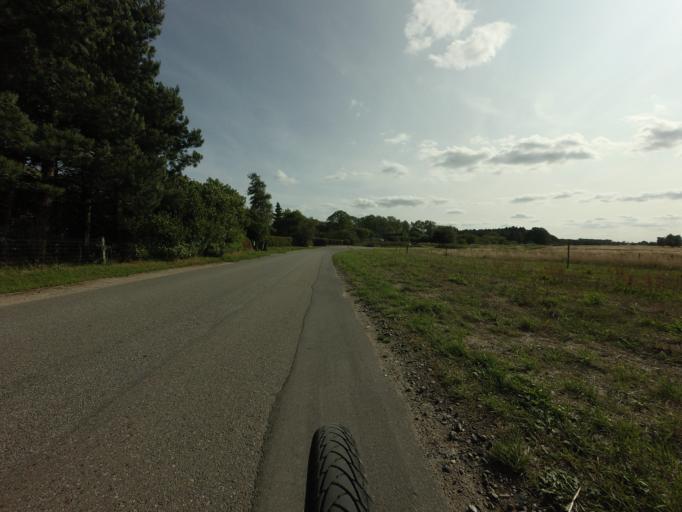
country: DK
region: Zealand
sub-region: Faxe Kommune
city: Fakse
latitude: 55.1848
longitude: 12.1127
